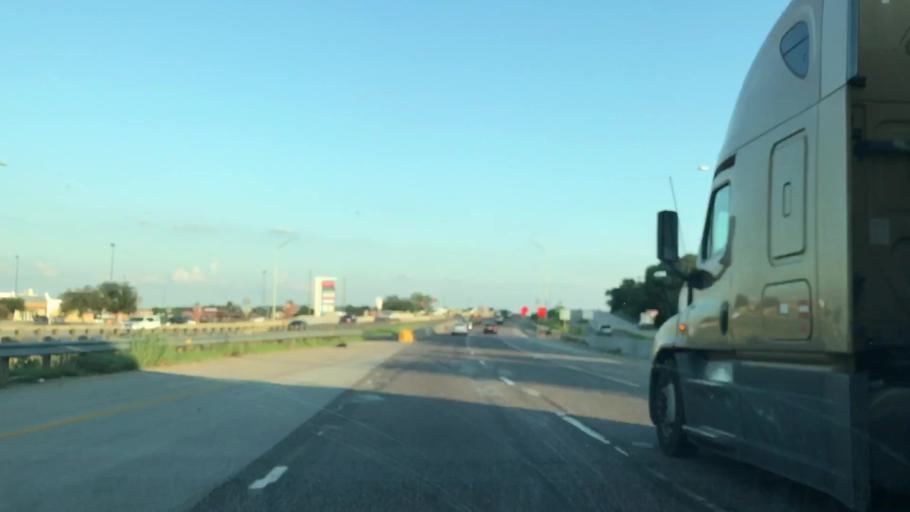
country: US
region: Texas
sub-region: Denton County
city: Denton
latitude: 33.1902
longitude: -97.1131
